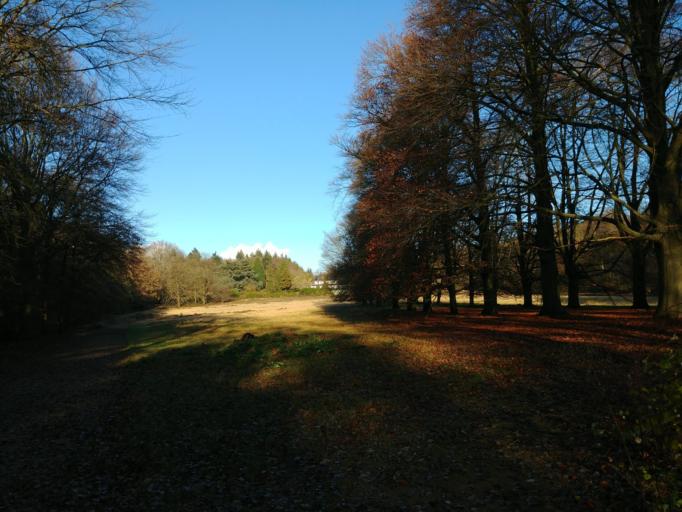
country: NL
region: Utrecht
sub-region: Gemeente Utrechtse Heuvelrug
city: Doorn
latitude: 52.0356
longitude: 5.3735
